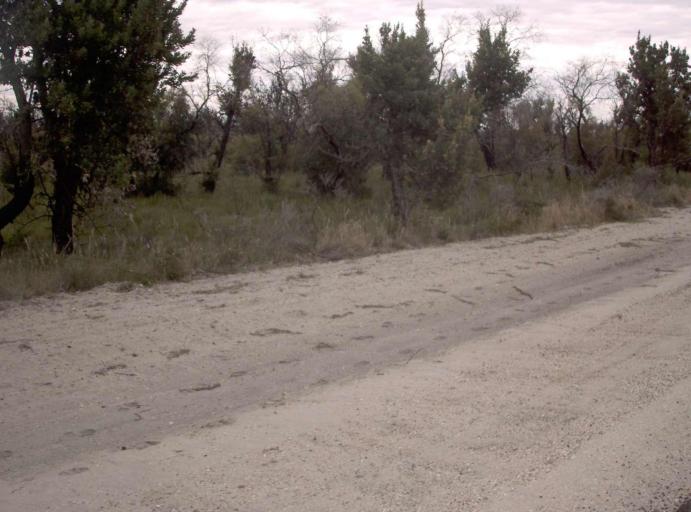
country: AU
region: Victoria
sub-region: East Gippsland
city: Bairnsdale
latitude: -38.1241
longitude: 147.4506
